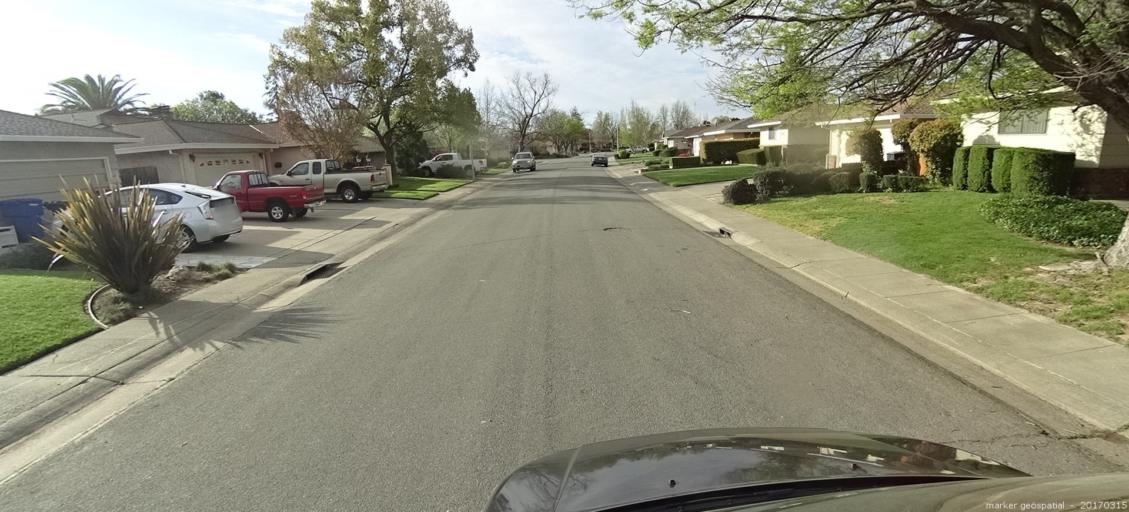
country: US
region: California
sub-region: Sacramento County
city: Parkway
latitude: 38.5096
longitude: -121.5084
